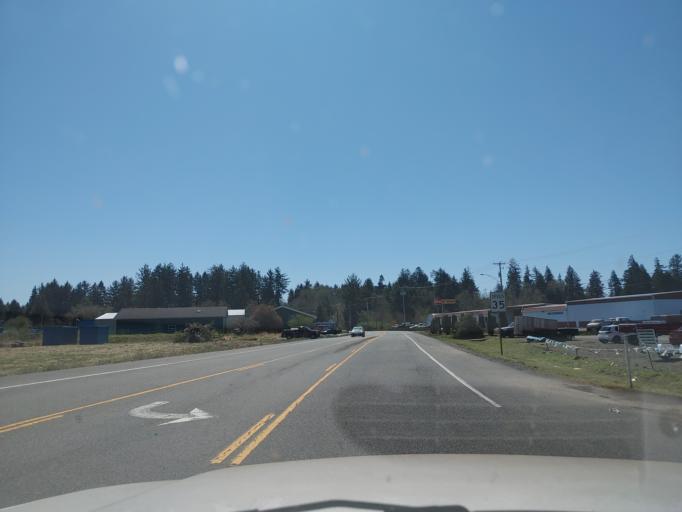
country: US
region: Oregon
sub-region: Clatsop County
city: Warrenton
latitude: 46.1566
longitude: -123.9045
